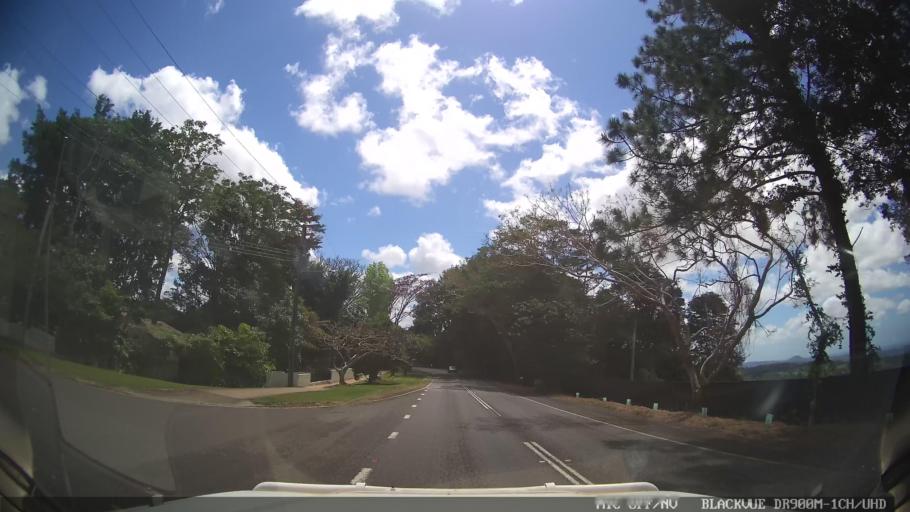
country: AU
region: Queensland
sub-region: Sunshine Coast
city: Nambour
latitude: -26.6619
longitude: 152.8833
